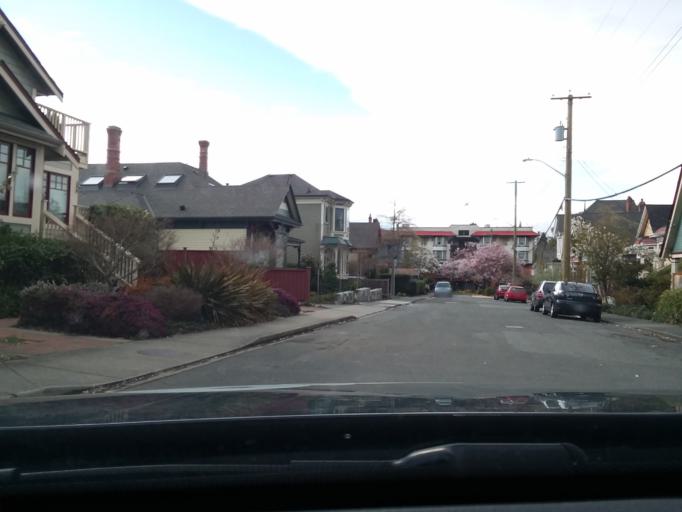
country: CA
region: British Columbia
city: Victoria
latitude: 48.4149
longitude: -123.3678
